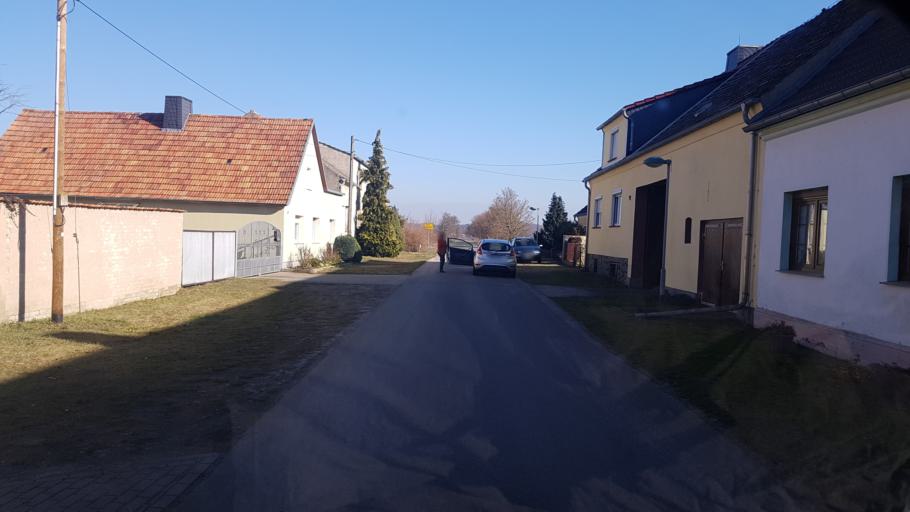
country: DE
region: Brandenburg
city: Ihlow
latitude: 51.8229
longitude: 13.3550
